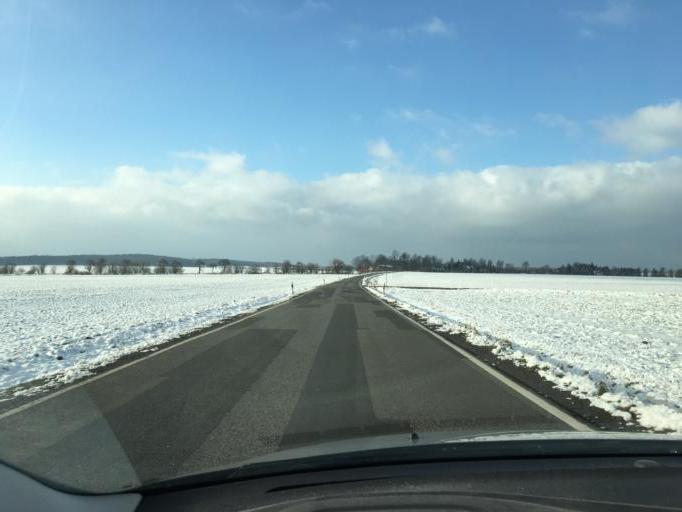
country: DE
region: Saxony
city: Grimma
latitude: 51.2521
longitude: 12.7010
